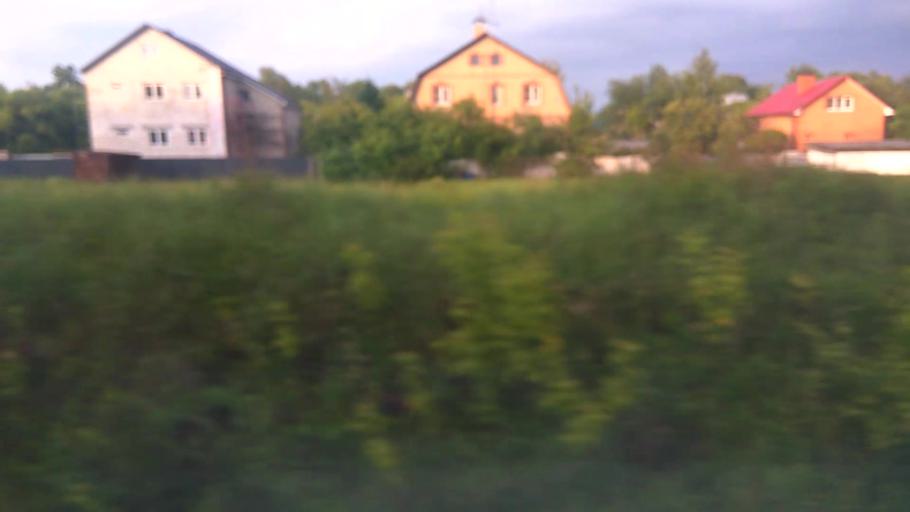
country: RU
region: Moskovskaya
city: Stupino
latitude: 54.8956
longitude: 38.0925
